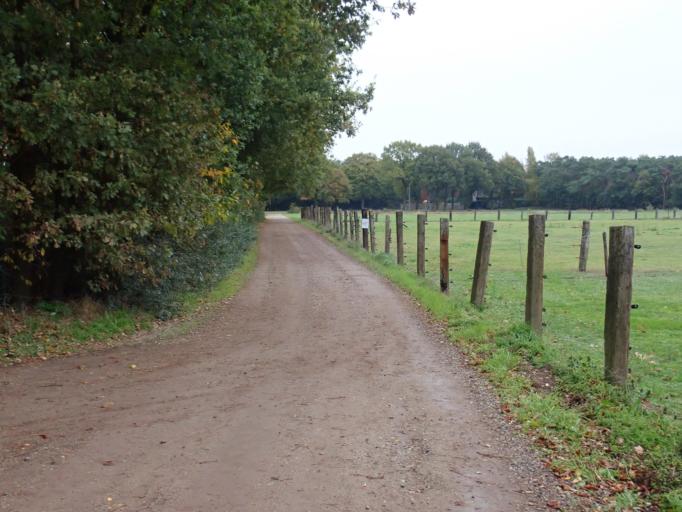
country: BE
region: Flanders
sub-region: Provincie Antwerpen
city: Wuustwezel
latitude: 51.3864
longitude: 4.5532
